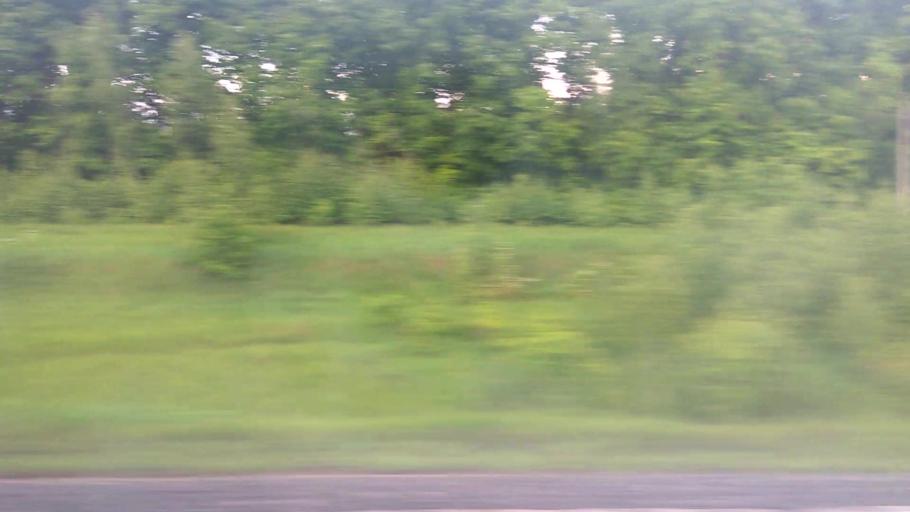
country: RU
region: Moskovskaya
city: Mikhnevo
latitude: 55.0708
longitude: 37.9825
